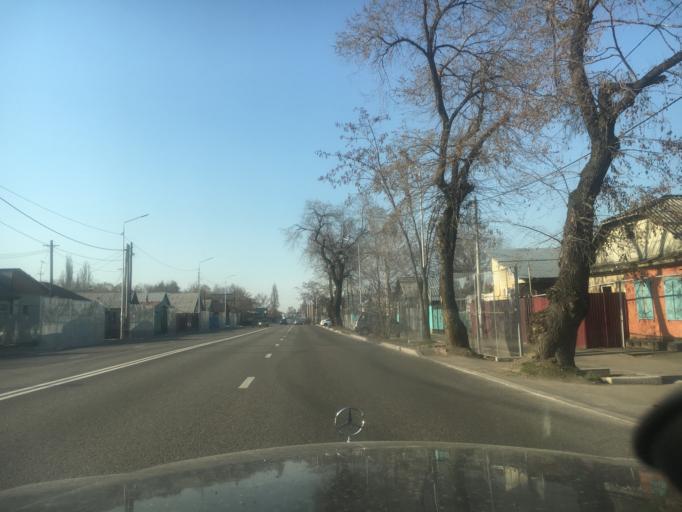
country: KZ
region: Almaty Qalasy
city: Almaty
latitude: 43.2802
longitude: 76.9401
